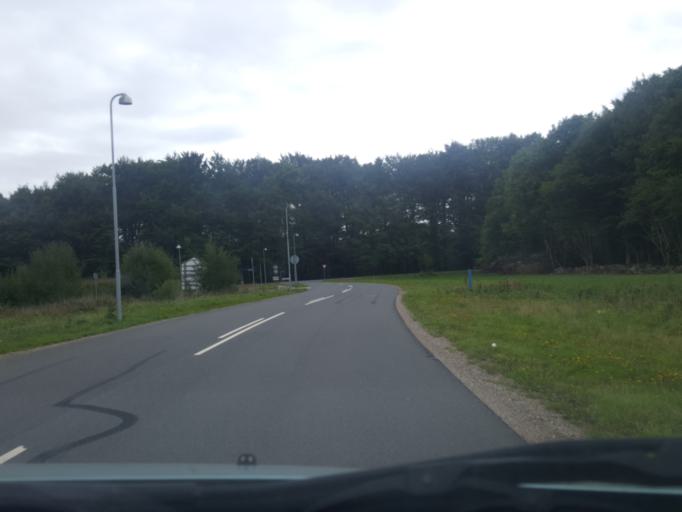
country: DK
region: Zealand
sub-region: Soro Kommune
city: Soro
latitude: 55.4429
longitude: 11.5262
